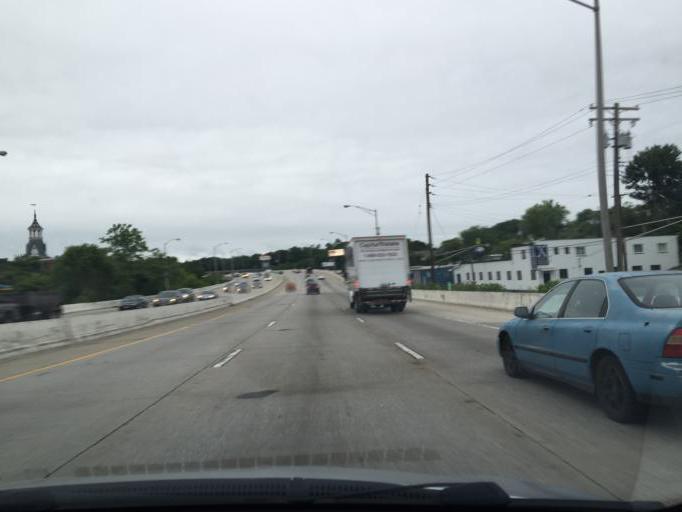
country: US
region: Maryland
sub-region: City of Baltimore
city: Baltimore
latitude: 39.3289
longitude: -76.6410
